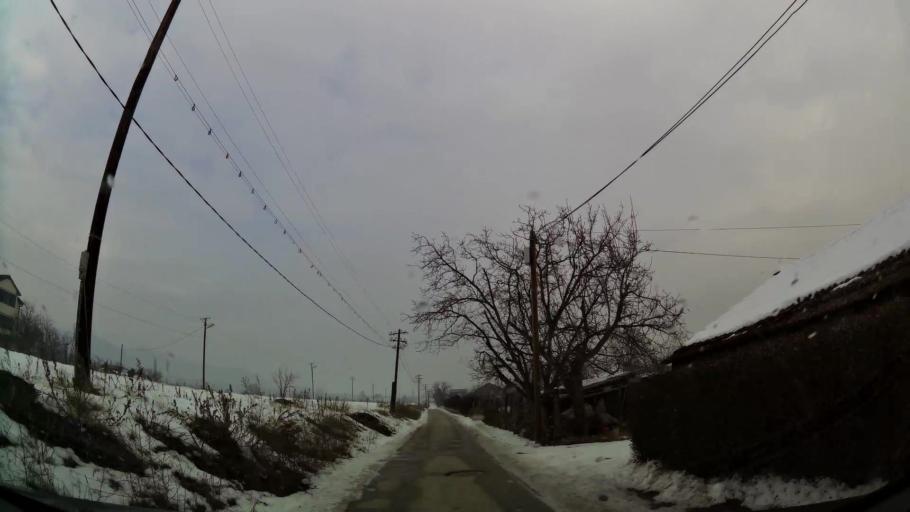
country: MK
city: Kondovo
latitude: 42.0481
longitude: 21.3544
